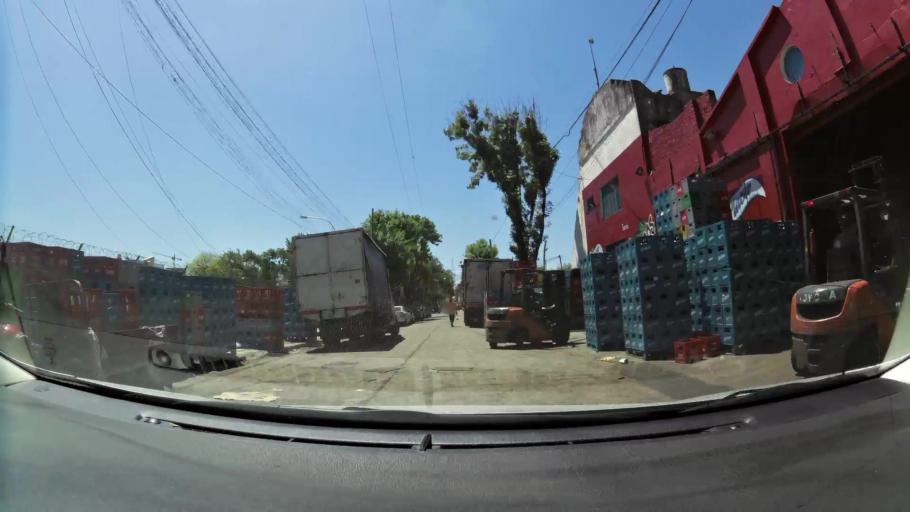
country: AR
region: Buenos Aires
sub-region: Partido de Avellaneda
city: Avellaneda
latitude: -34.6491
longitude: -58.3925
